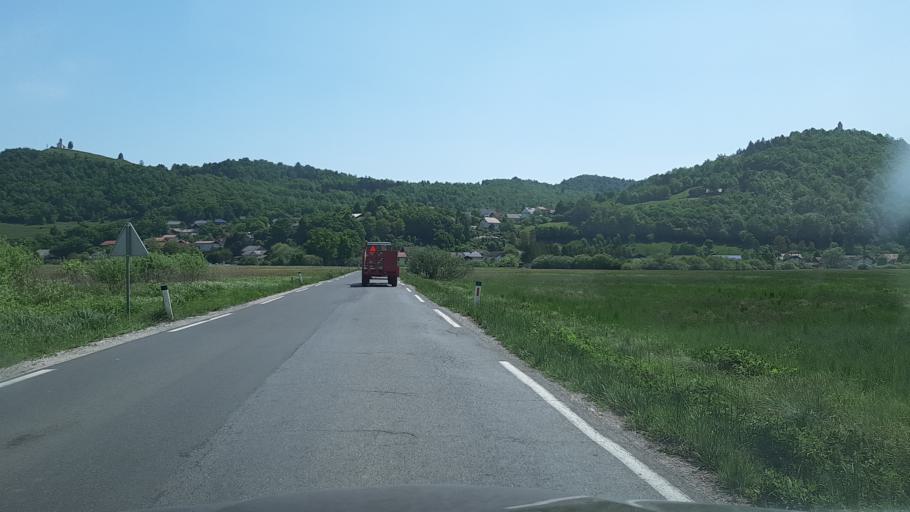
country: SI
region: Brezovica
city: Notranje Gorice
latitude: 45.9662
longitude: 14.4050
